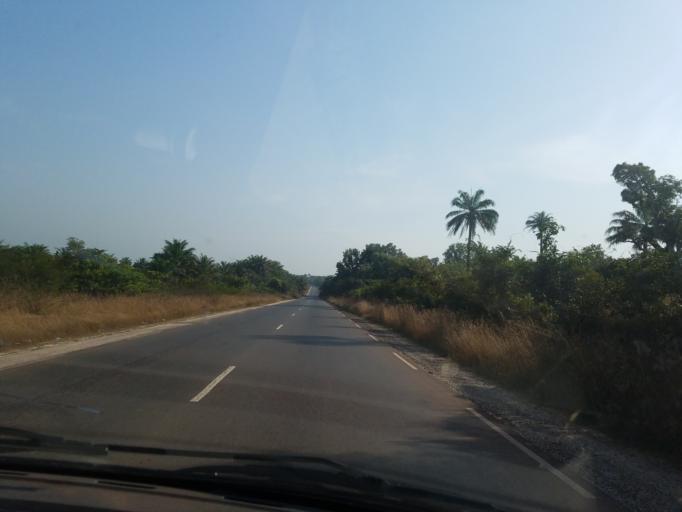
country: GN
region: Boke
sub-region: Boke Prefecture
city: Sangueya
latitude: 10.7515
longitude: -14.3802
